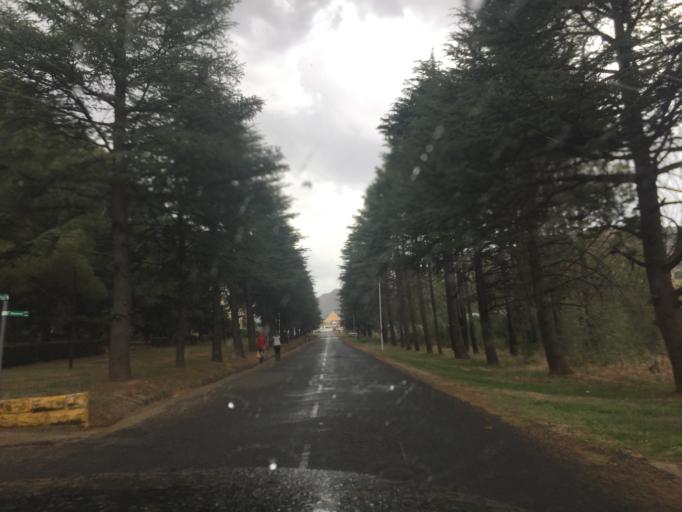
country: LS
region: Maseru
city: Nako
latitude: -29.4485
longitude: 27.7202
